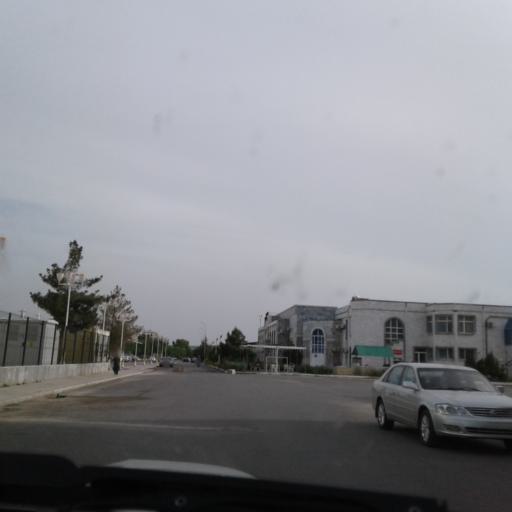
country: TM
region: Mary
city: Mary
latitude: 37.5933
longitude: 61.8359
